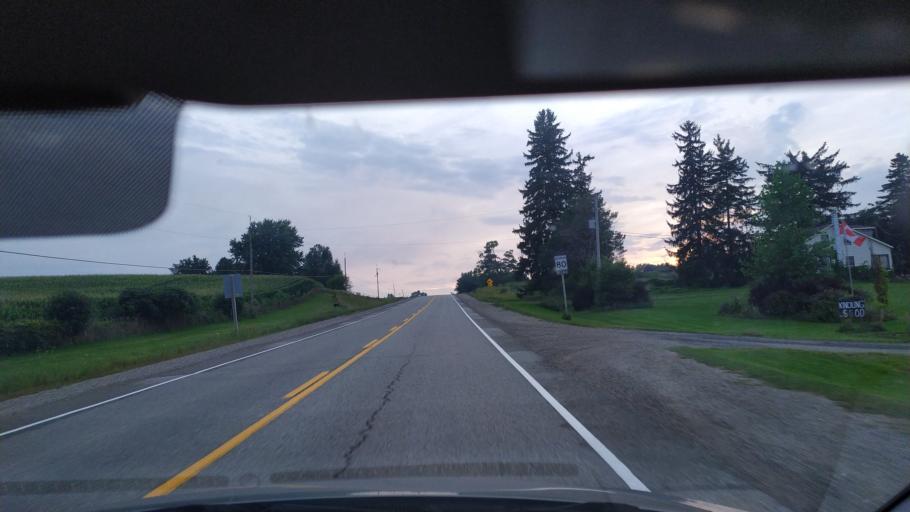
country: CA
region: Ontario
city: Kitchener
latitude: 43.3088
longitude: -80.5859
